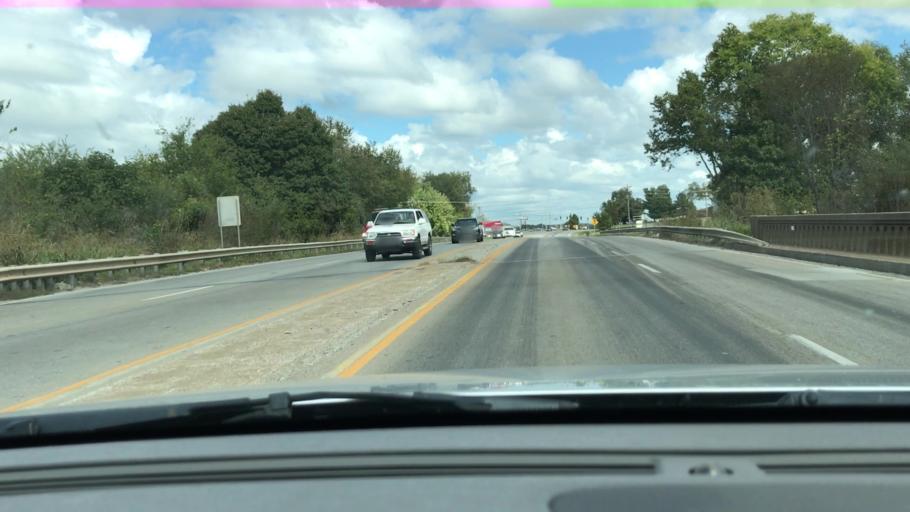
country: US
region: Kentucky
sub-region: Warren County
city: Bowling Green
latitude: 37.0128
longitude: -86.3793
